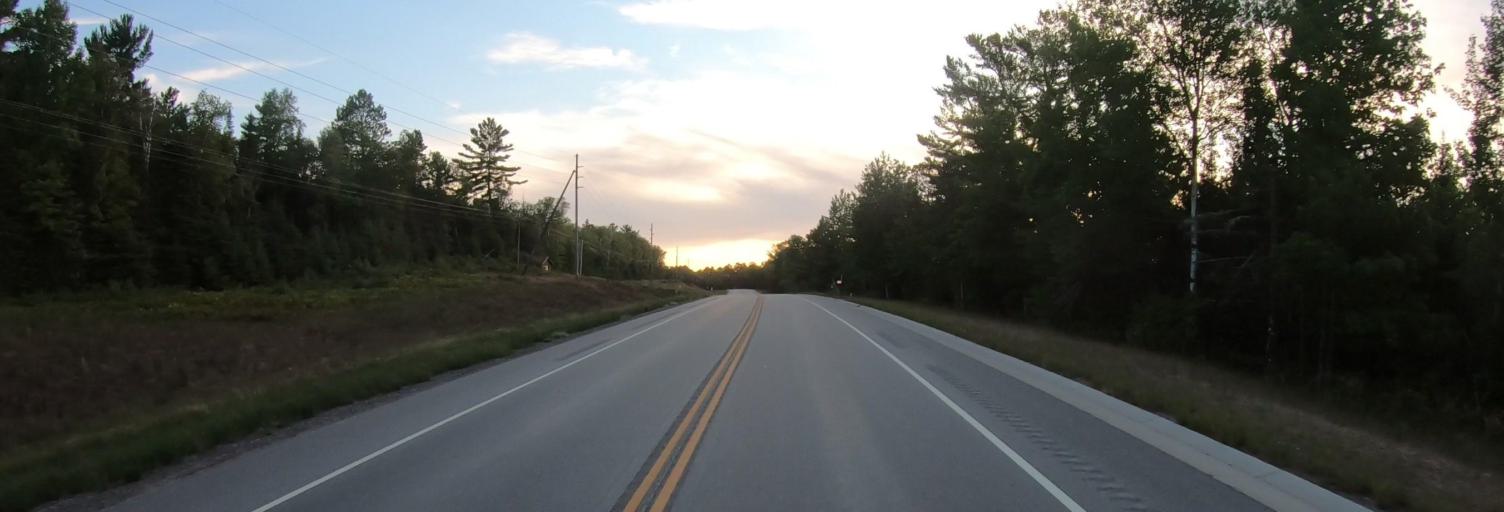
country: US
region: Minnesota
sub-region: Saint Louis County
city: Babbitt
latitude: 47.8573
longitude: -92.0704
